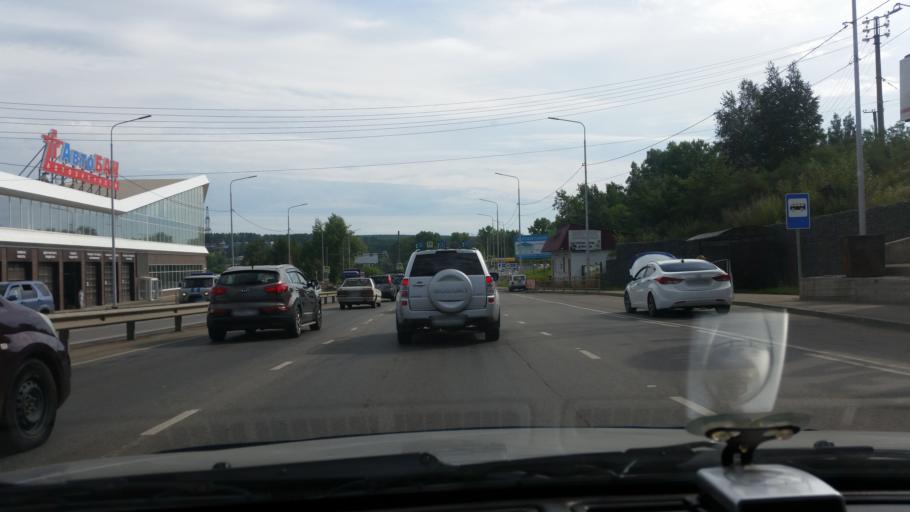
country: RU
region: Irkutsk
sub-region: Irkutskiy Rayon
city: Irkutsk
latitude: 52.3306
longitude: 104.3145
